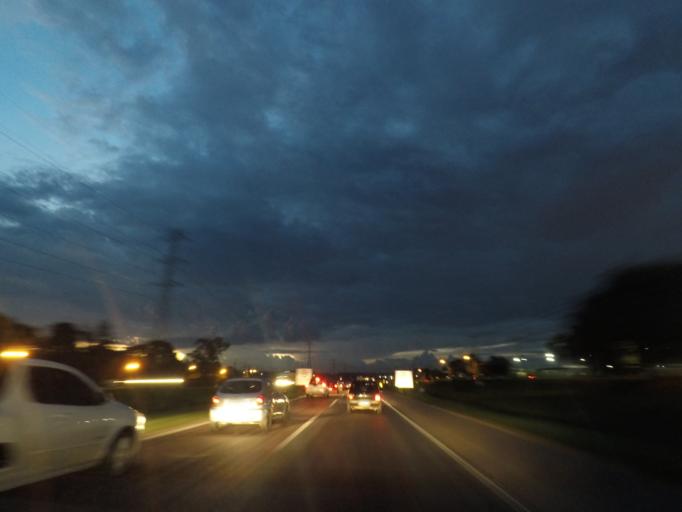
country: BR
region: Parana
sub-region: Araucaria
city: Araucaria
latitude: -25.5274
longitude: -49.3283
